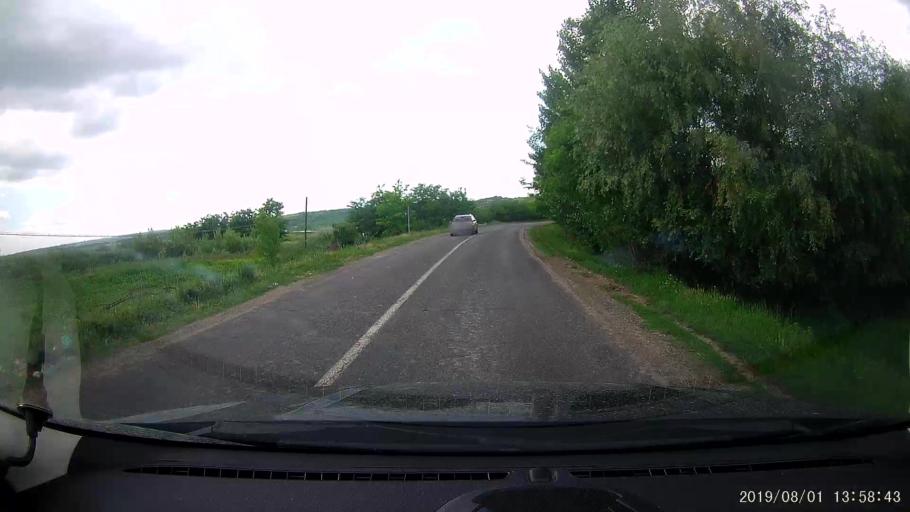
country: RO
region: Galati
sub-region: Comuna Foltesti
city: Foltesti
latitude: 45.7822
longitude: 28.0837
